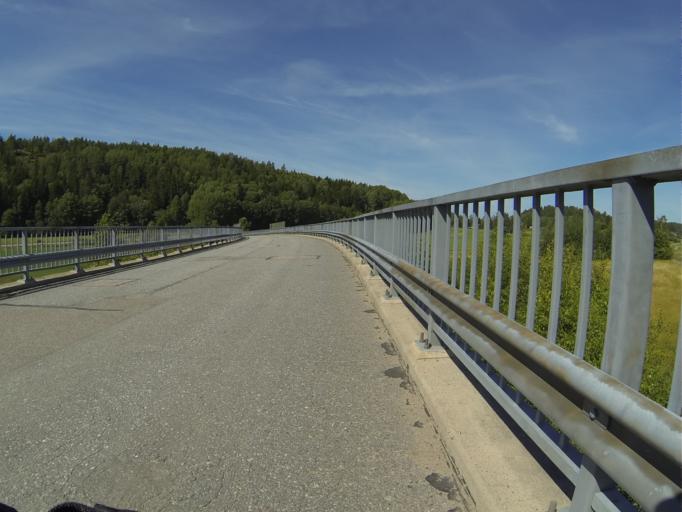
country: FI
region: Varsinais-Suomi
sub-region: Salo
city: Salo
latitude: 60.3055
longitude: 23.1086
